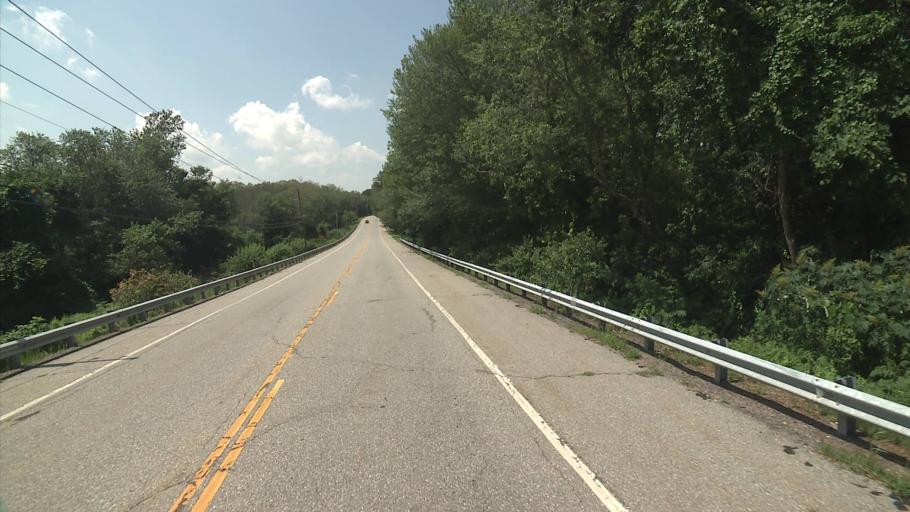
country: US
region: Connecticut
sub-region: New London County
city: Preston City
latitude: 41.5347
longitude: -72.0222
